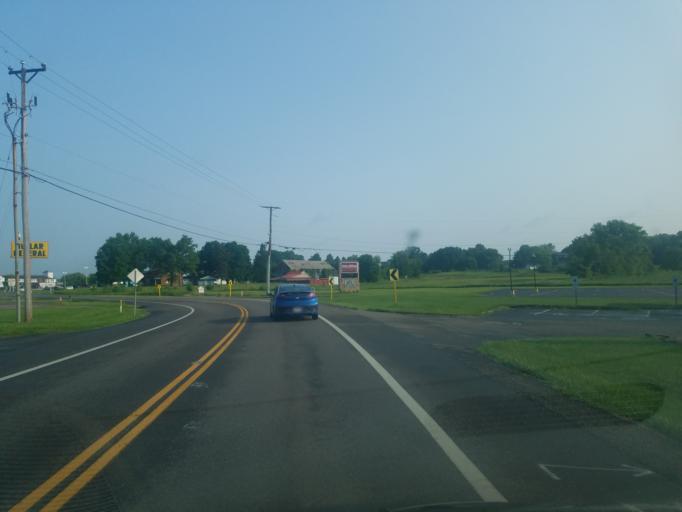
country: US
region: Ohio
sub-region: Tuscarawas County
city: Strasburg
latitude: 40.6383
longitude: -81.4401
